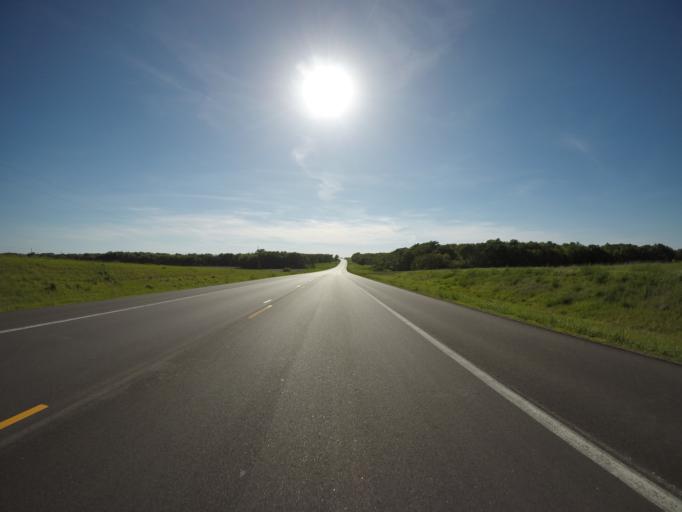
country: US
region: Kansas
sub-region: Clay County
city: Clay Center
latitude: 39.3794
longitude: -96.9687
